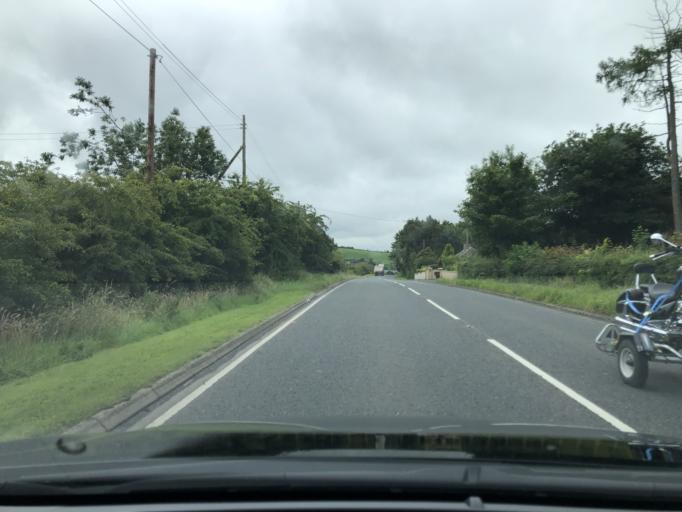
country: GB
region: Northern Ireland
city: Ballynahinch
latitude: 54.3875
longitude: -5.8812
